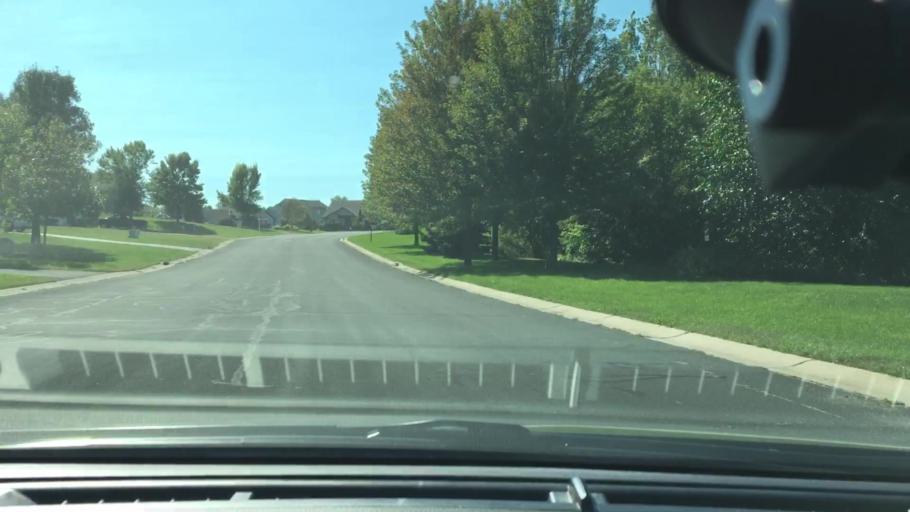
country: US
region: Minnesota
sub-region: Wright County
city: Hanover
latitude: 45.1648
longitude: -93.6775
